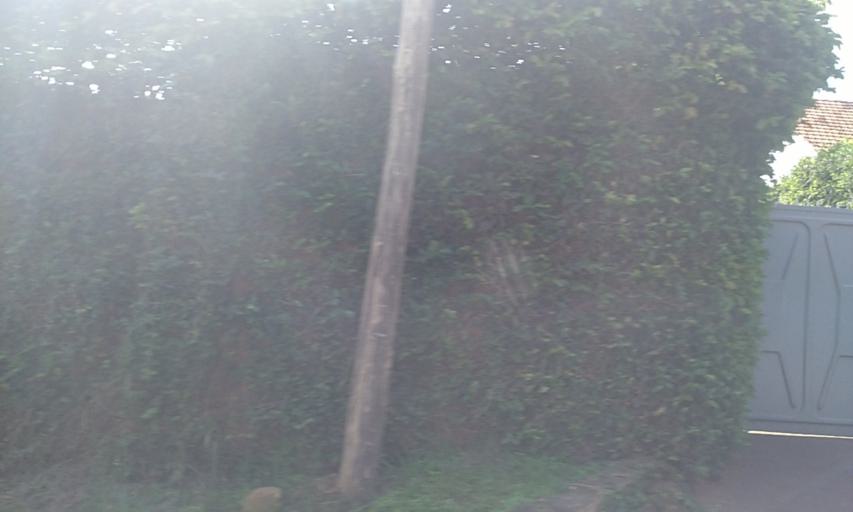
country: UG
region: Central Region
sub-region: Wakiso District
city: Kireka
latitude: 0.3544
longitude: 32.6191
